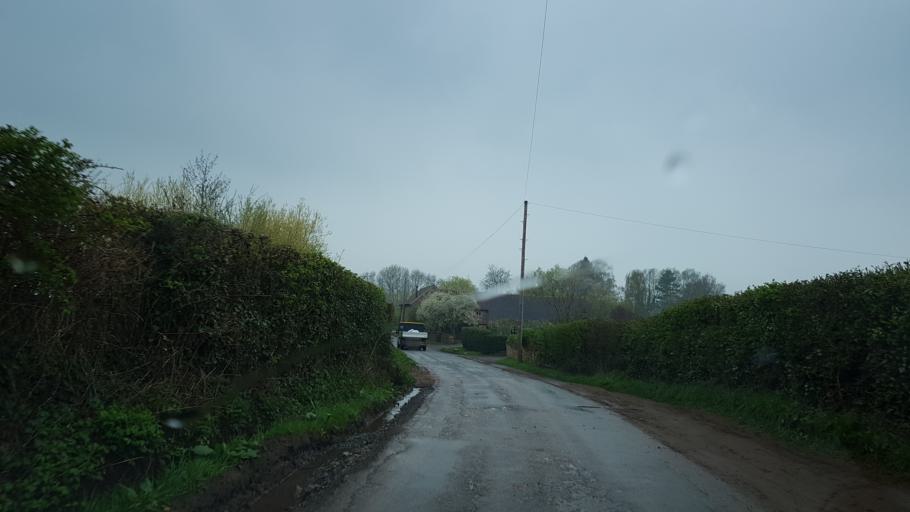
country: GB
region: England
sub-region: Herefordshire
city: Ledbury
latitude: 52.0684
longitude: -2.4407
